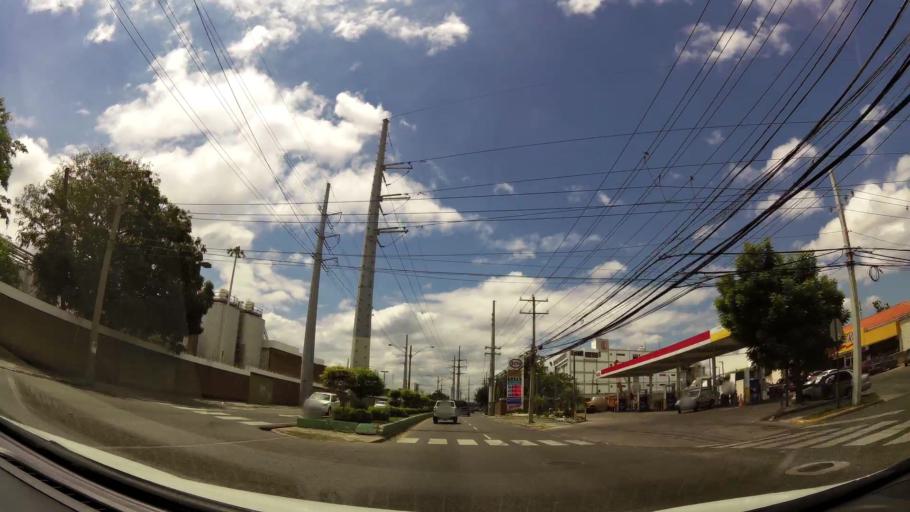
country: DO
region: Nacional
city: Bella Vista
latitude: 18.4421
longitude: -69.9424
